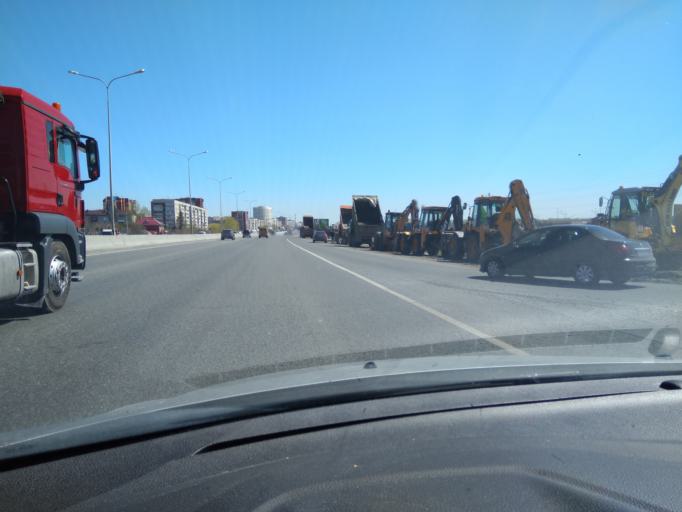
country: RU
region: Tjumen
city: Tyumen
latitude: 57.1229
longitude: 65.5089
